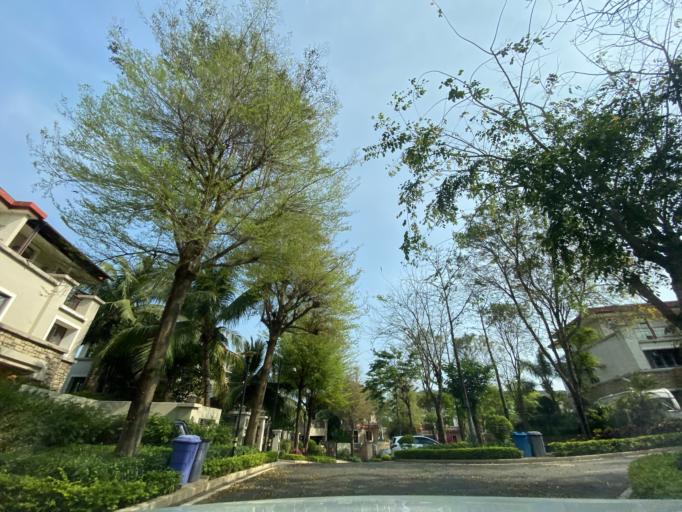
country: CN
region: Hainan
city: Yingzhou
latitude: 18.4102
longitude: 109.8453
